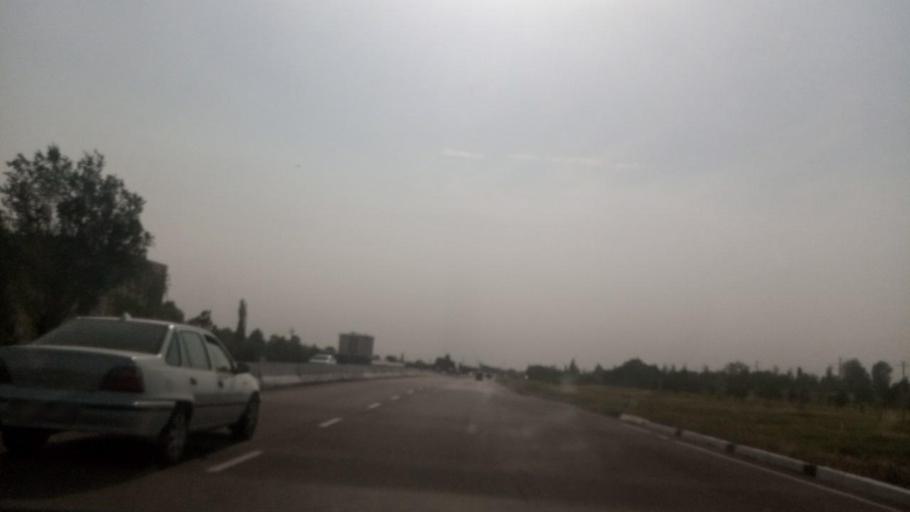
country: UZ
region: Toshkent
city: Ohangaron
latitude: 40.9103
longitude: 69.8096
